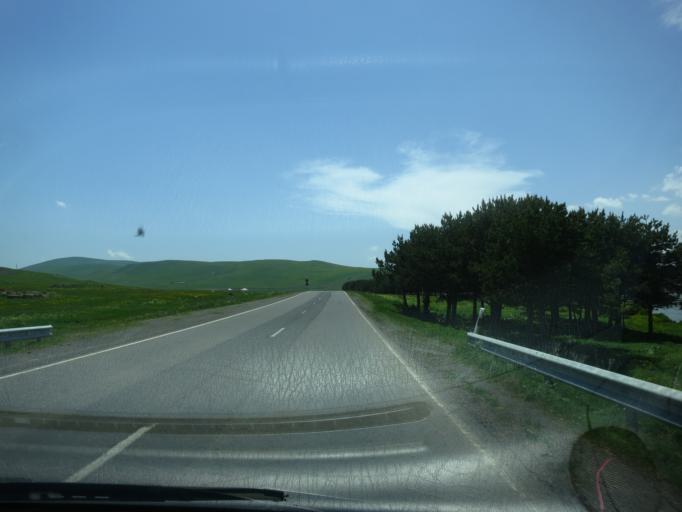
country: GE
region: Samtskhe-Javakheti
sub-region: Ninotsminda
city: Ninotsminda
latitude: 41.3045
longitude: 43.7594
